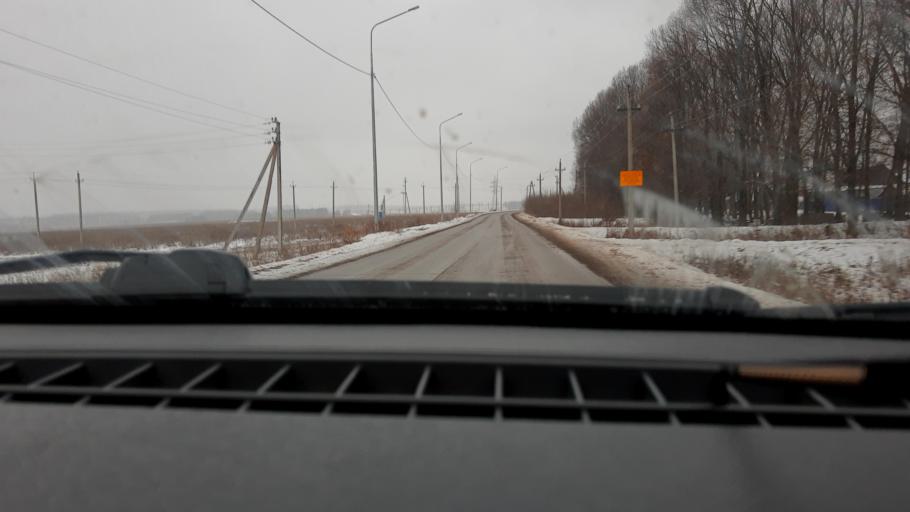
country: RU
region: Bashkortostan
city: Kabakovo
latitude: 54.7020
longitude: 56.2243
